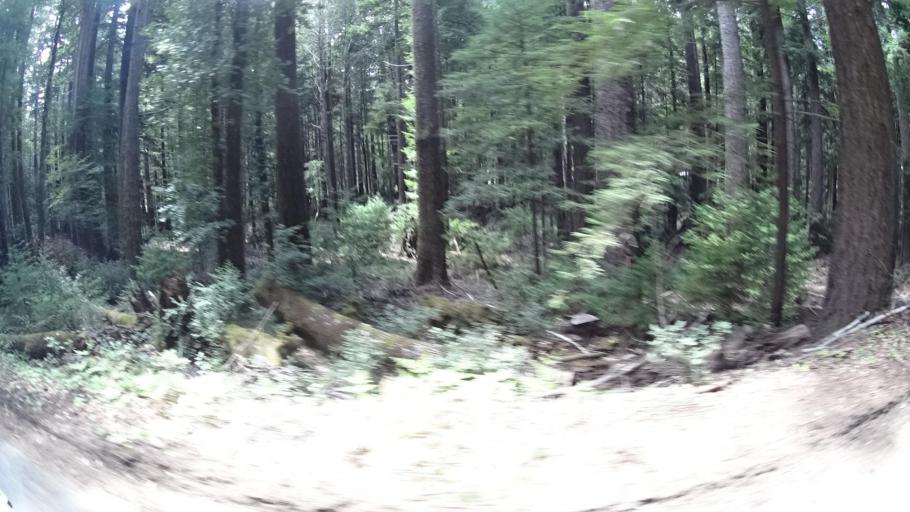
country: US
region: California
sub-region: Humboldt County
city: Redway
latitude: 40.0266
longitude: -123.9474
